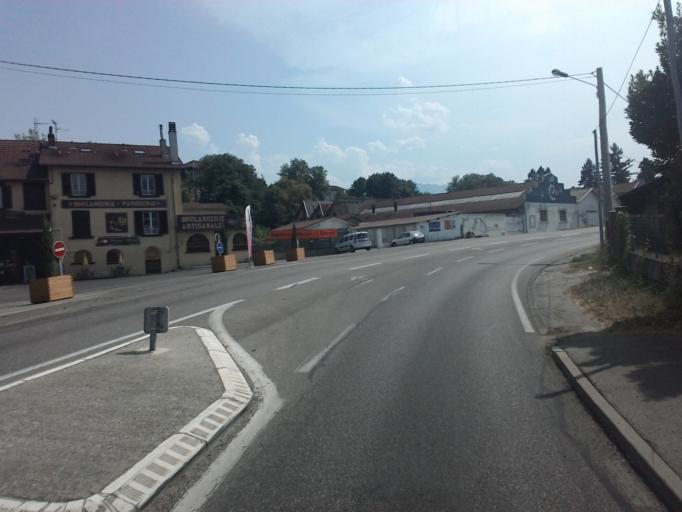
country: FR
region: Rhone-Alpes
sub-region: Departement de l'Isere
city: Voiron
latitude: 45.3584
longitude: 5.6012
